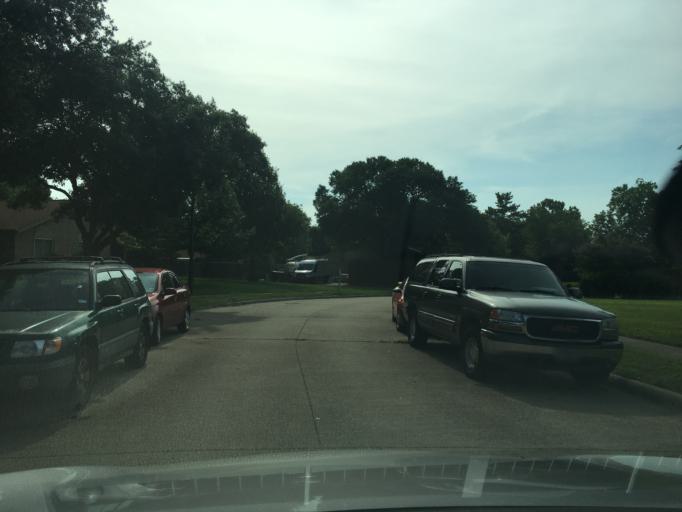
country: US
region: Texas
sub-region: Dallas County
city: Richardson
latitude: 32.9674
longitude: -96.6783
